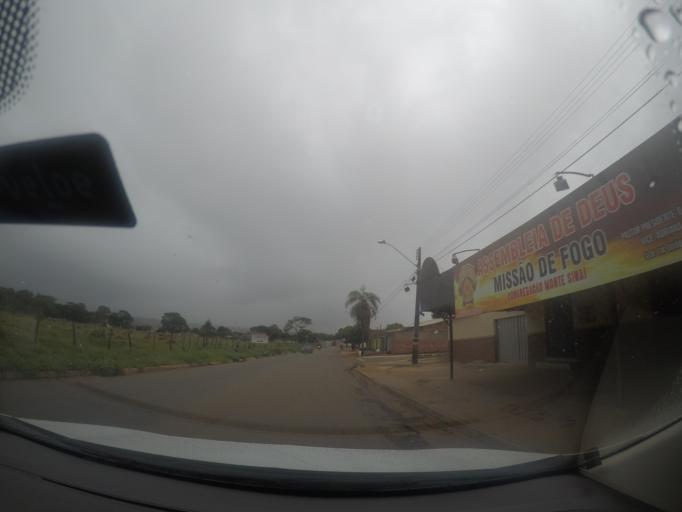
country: BR
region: Goias
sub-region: Goiania
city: Goiania
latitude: -16.6150
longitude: -49.3533
